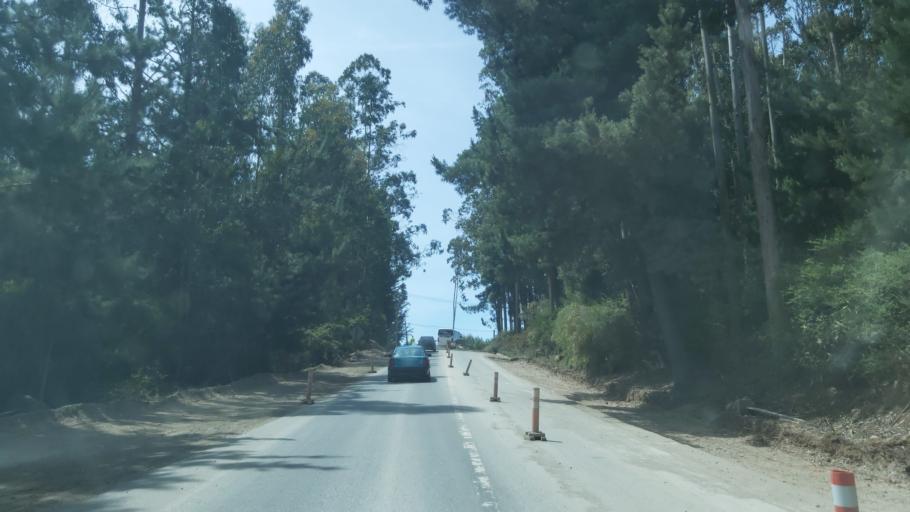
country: CL
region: Maule
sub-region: Provincia de Talca
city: Constitucion
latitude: -35.3772
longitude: -72.4218
